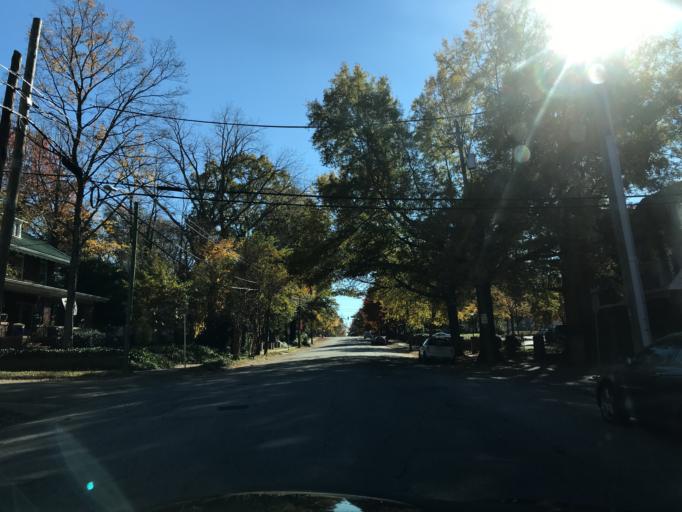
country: US
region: North Carolina
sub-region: Wake County
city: Raleigh
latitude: 35.7894
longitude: -78.6360
